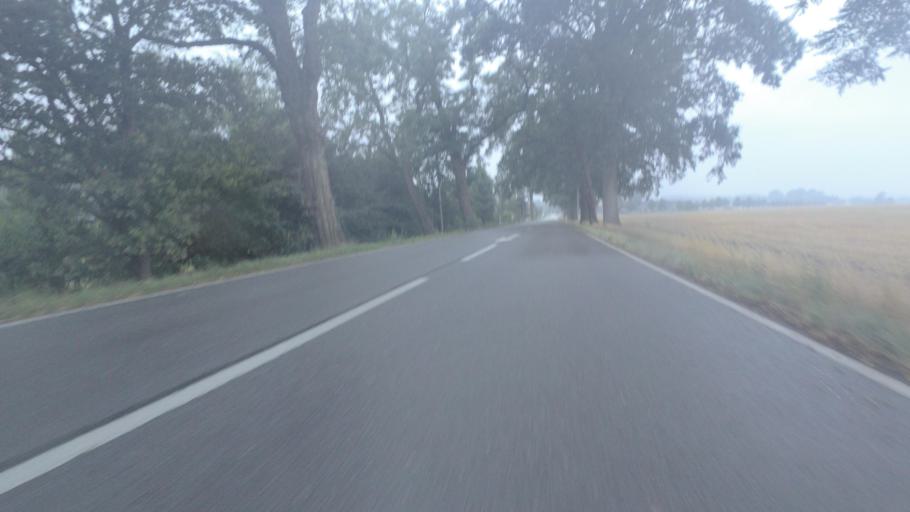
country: DE
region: Brandenburg
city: Heiligengrabe
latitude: 53.0854
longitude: 12.3490
